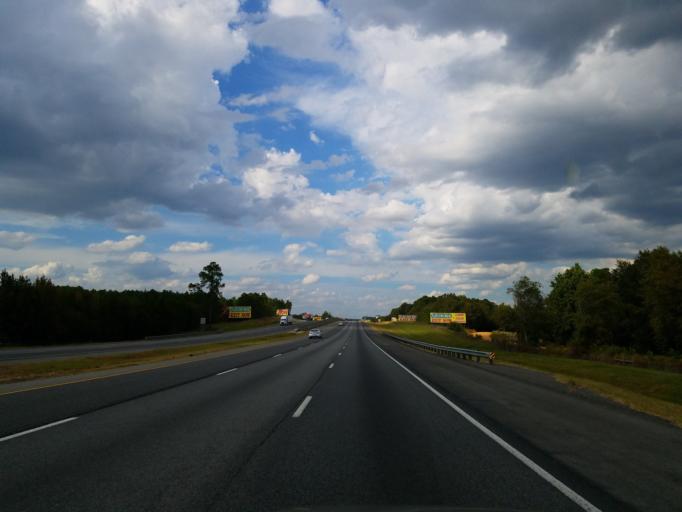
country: US
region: Georgia
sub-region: Turner County
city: Ashburn
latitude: 31.8197
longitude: -83.7095
